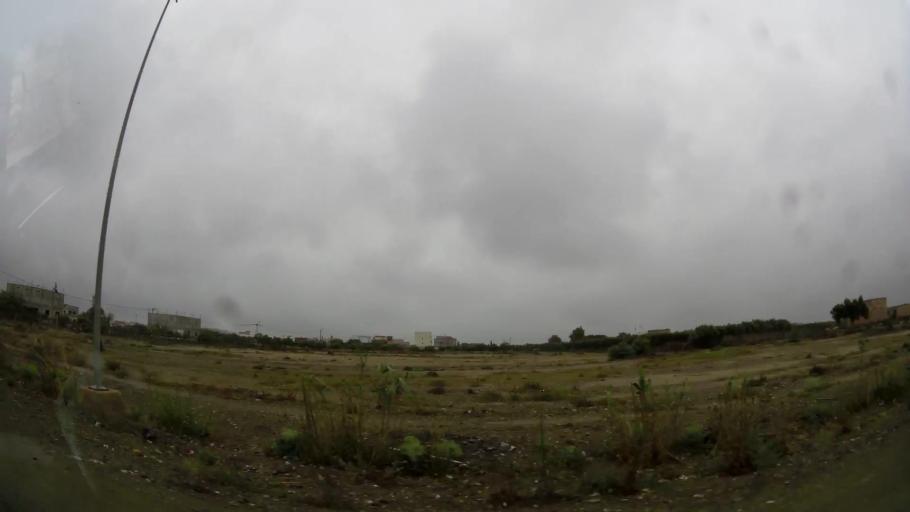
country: MA
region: Taza-Al Hoceima-Taounate
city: Imzourene
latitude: 35.1544
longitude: -3.8309
